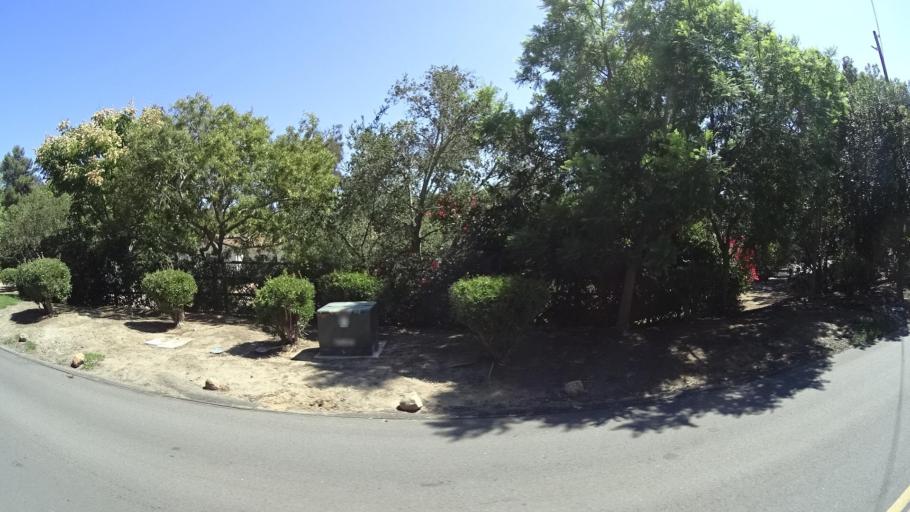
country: US
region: California
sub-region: San Diego County
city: Rancho Santa Fe
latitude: 33.0305
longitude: -117.2016
